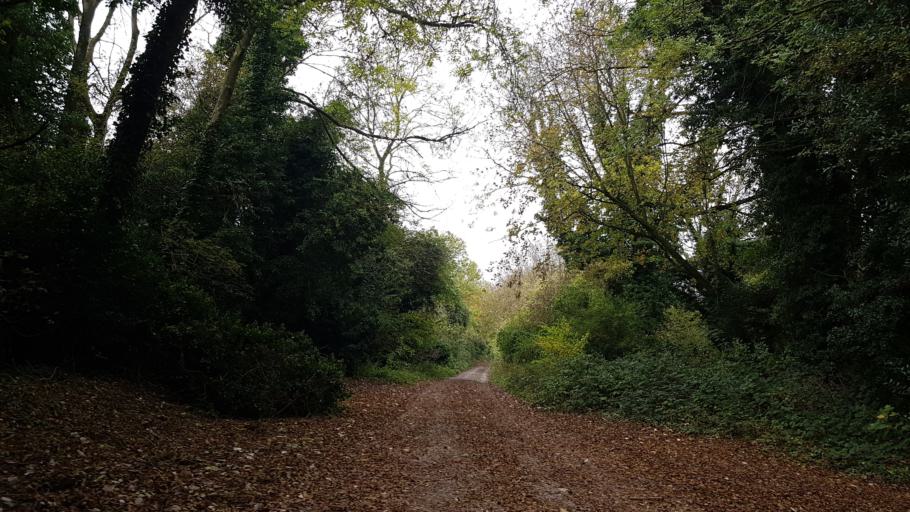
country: GB
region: England
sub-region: Surrey
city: Guildford
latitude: 51.2288
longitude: -0.6058
